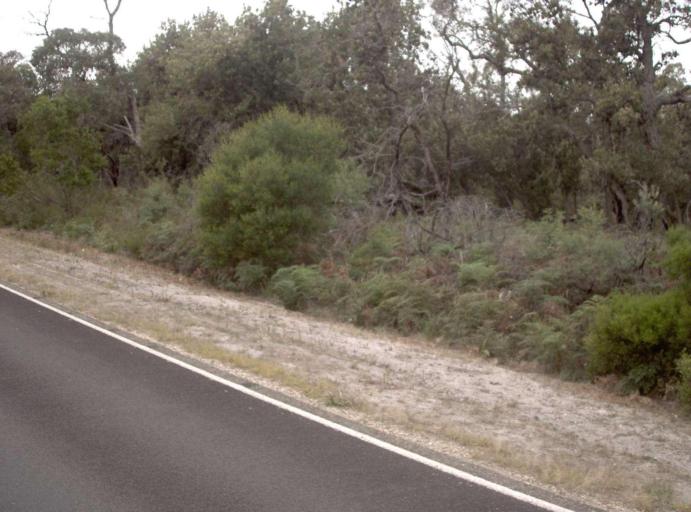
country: AU
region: Victoria
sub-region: East Gippsland
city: Bairnsdale
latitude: -38.0718
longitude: 147.5468
